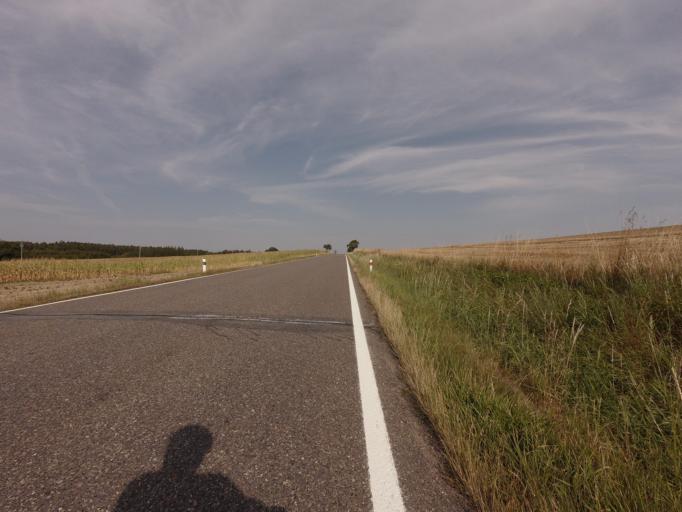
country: CZ
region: Central Bohemia
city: Petrovice
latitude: 49.5100
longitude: 14.3623
